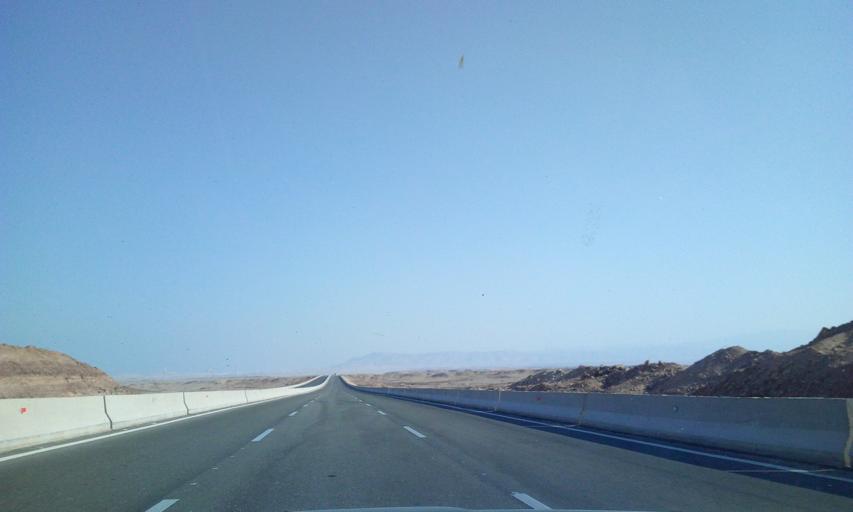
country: EG
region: As Suways
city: Ain Sukhna
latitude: 29.1872
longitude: 32.5000
